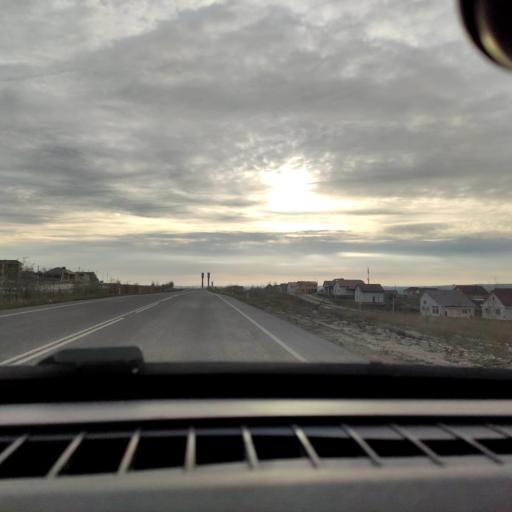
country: RU
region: Belgorod
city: Ilovka
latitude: 50.6492
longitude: 38.6247
